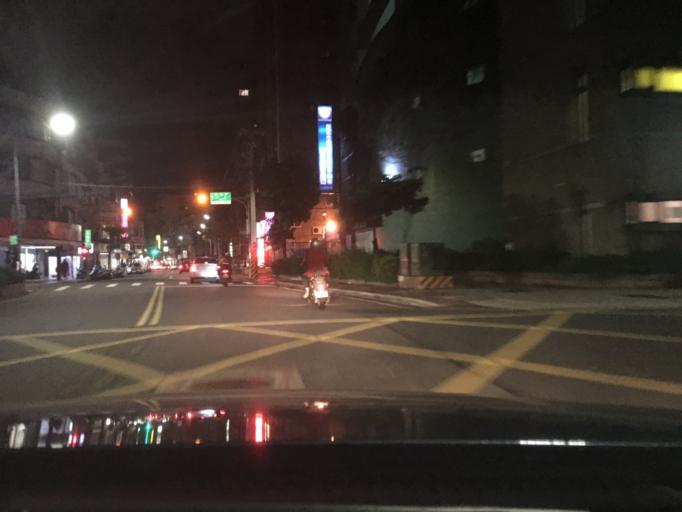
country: TW
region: Taipei
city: Taipei
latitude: 25.0855
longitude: 121.4770
